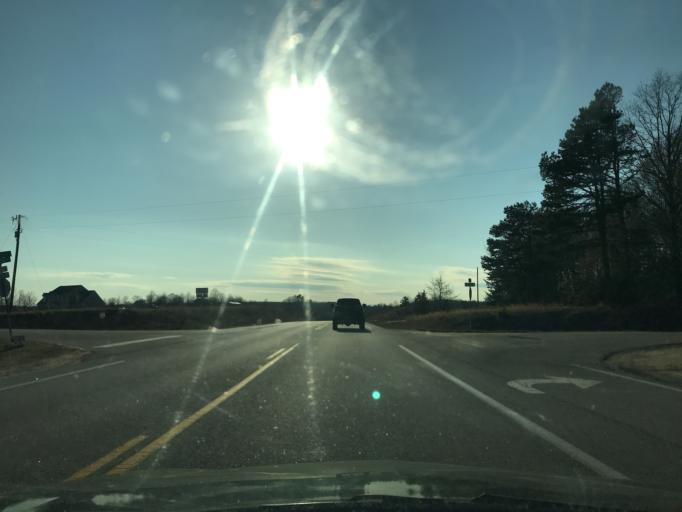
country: US
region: Virginia
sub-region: Nottoway County
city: Crewe
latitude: 37.2786
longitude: -78.2142
